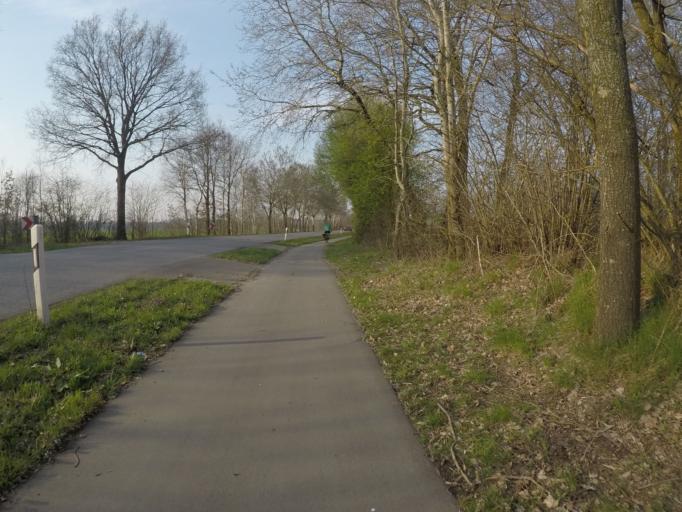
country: DE
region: Schleswig-Holstein
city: Wahlstedt
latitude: 53.9712
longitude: 10.1878
